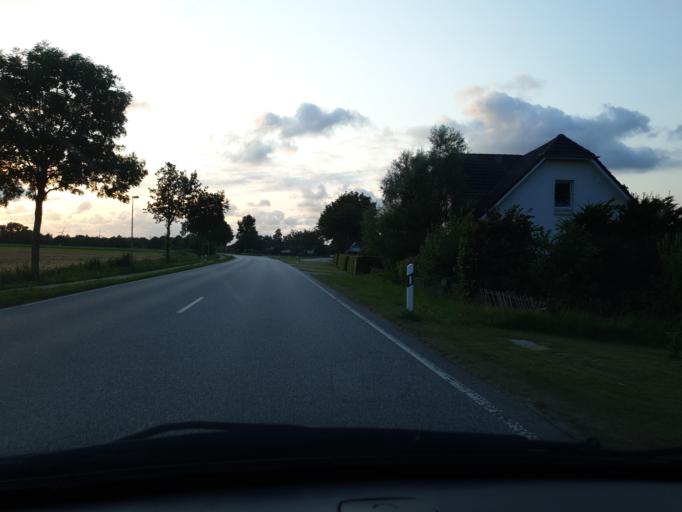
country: DE
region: Schleswig-Holstein
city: Diekhusen-Fahrstedt
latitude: 53.9394
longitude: 9.0259
